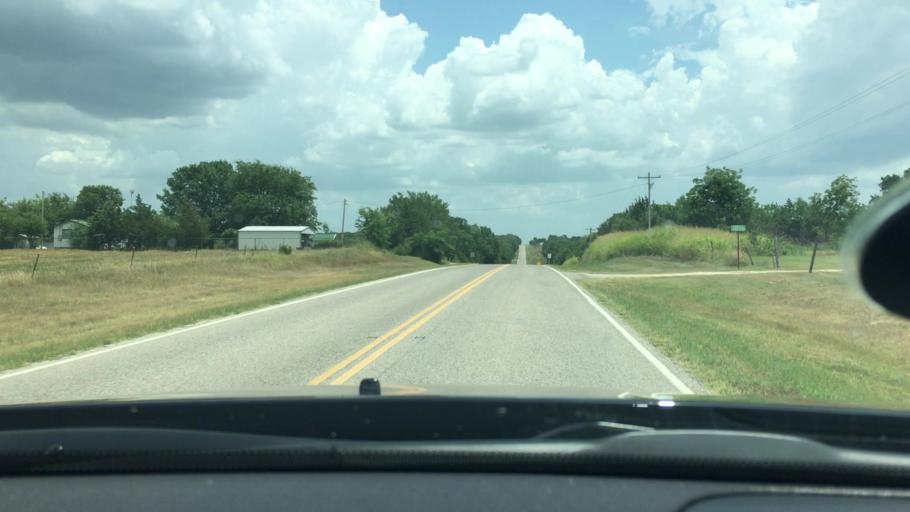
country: US
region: Oklahoma
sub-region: Love County
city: Marietta
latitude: 33.9839
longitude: -96.9807
